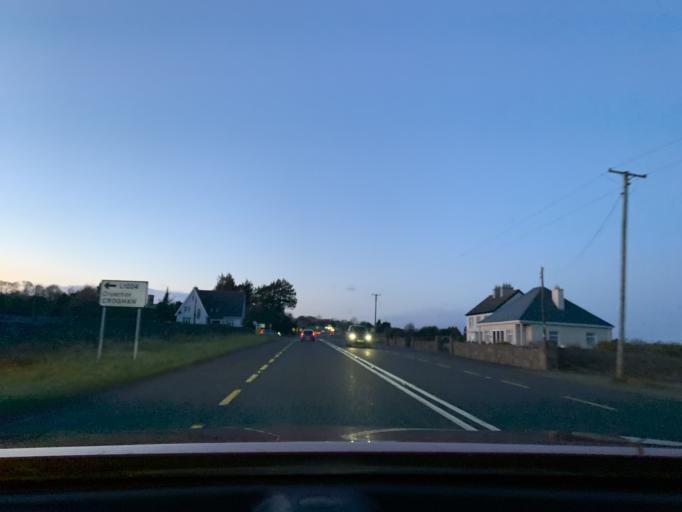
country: IE
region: Connaught
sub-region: Roscommon
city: Boyle
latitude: 53.9654
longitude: -8.1975
